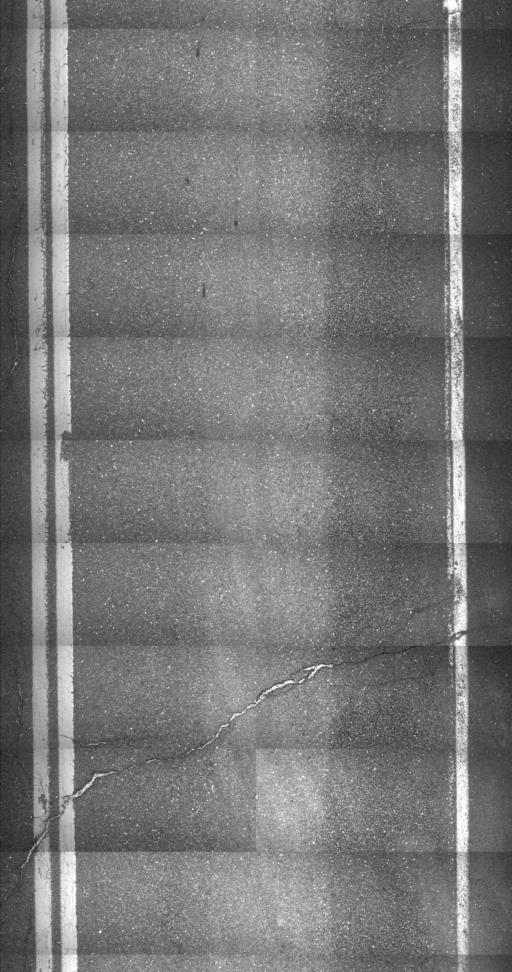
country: US
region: New Hampshire
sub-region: Sullivan County
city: Claremont
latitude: 43.3539
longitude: -72.4071
